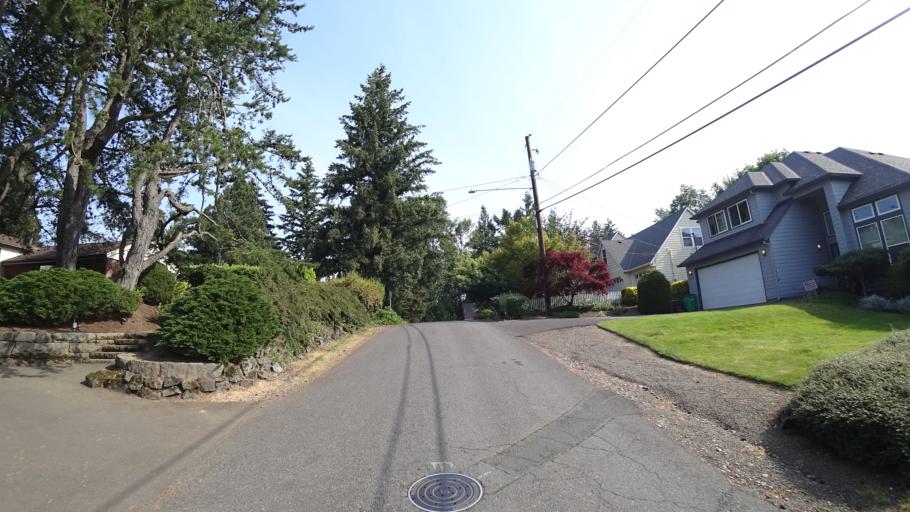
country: US
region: Oregon
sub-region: Washington County
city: Garden Home-Whitford
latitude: 45.4612
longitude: -122.7148
